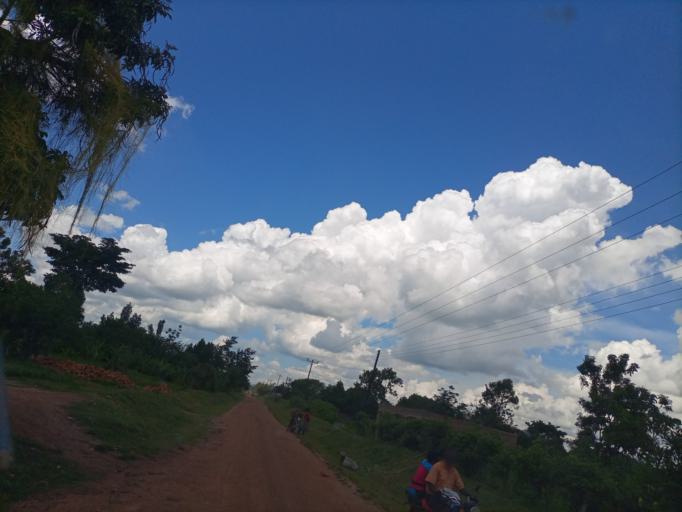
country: UG
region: Eastern Region
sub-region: Tororo District
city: Tororo
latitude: 0.6728
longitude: 34.0046
